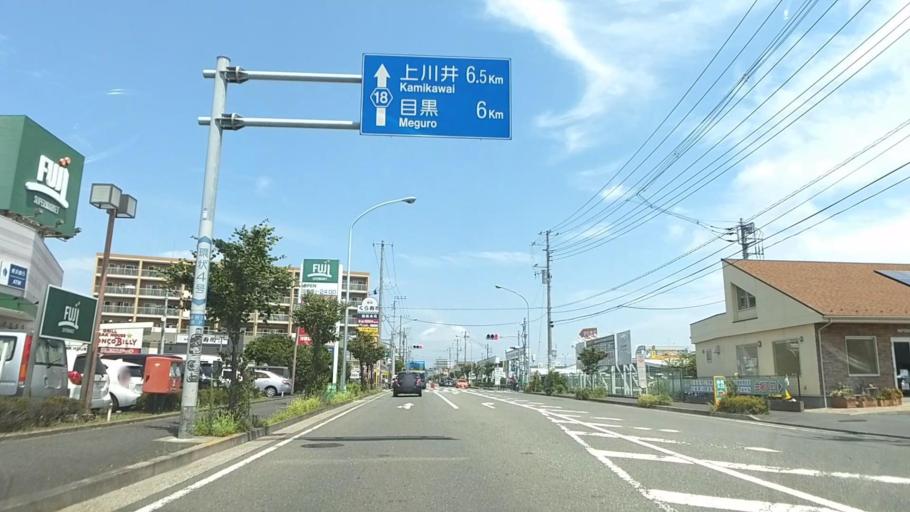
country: JP
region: Kanagawa
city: Minami-rinkan
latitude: 35.4601
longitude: 139.4805
